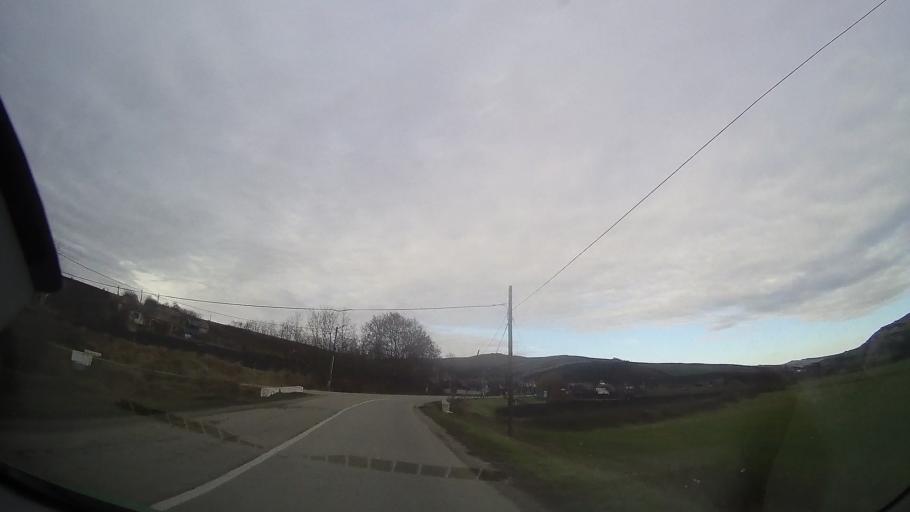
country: RO
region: Cluj
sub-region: Comuna Camarasu
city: Camarasu
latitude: 46.8160
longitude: 24.1394
